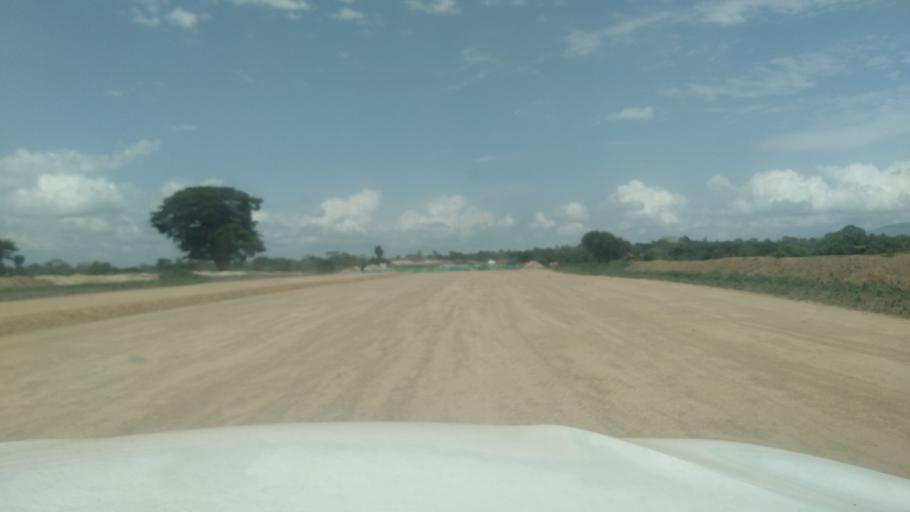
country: ET
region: Oromiya
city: Shashemene
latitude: 7.2723
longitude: 38.6002
